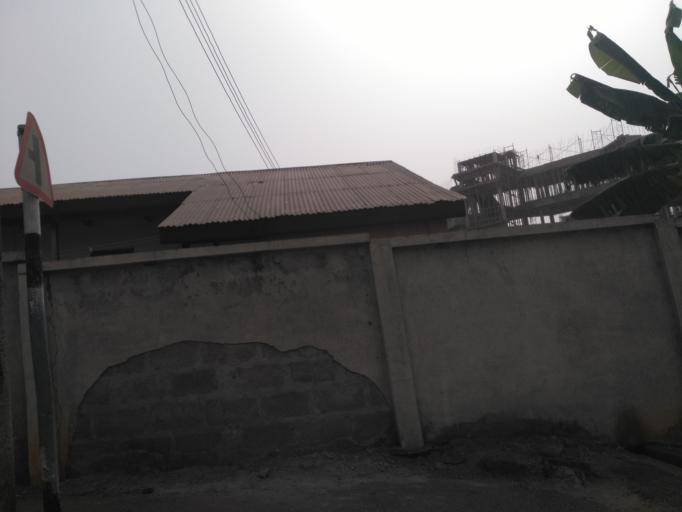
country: GH
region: Ashanti
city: Kumasi
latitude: 6.6875
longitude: -1.6217
